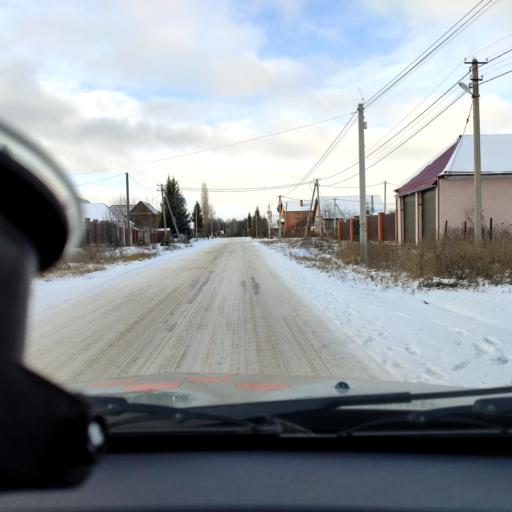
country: RU
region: Bashkortostan
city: Avdon
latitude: 54.7850
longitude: 55.7259
